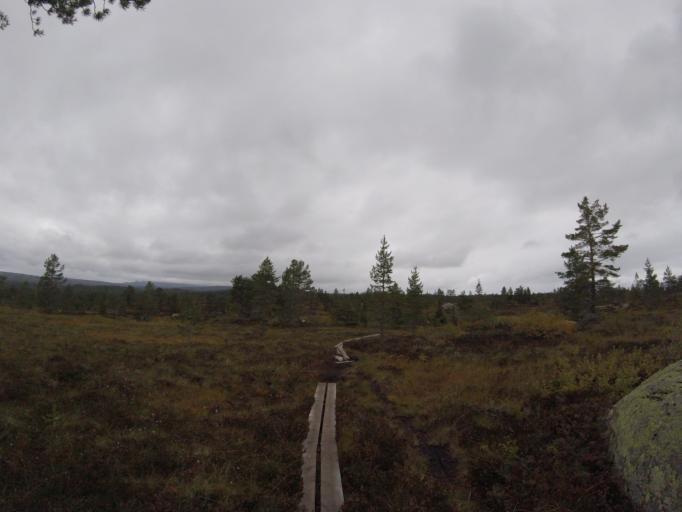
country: NO
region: Buskerud
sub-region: Flesberg
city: Lampeland
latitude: 59.7581
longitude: 9.4012
